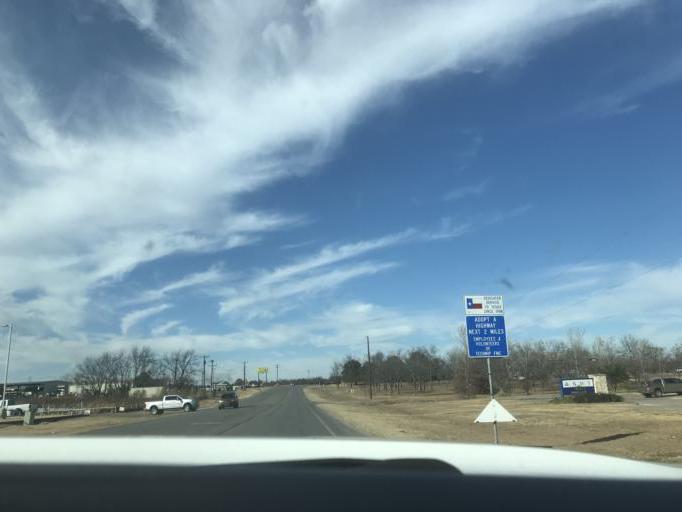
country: US
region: Texas
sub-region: Erath County
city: Stephenville
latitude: 32.2032
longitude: -98.2464
